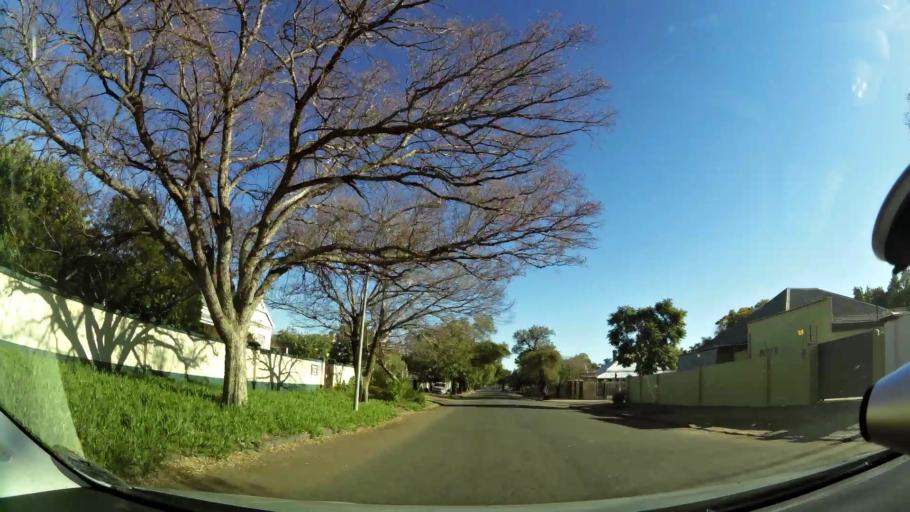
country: ZA
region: Northern Cape
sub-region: Frances Baard District Municipality
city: Kimberley
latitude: -28.7471
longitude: 24.7766
